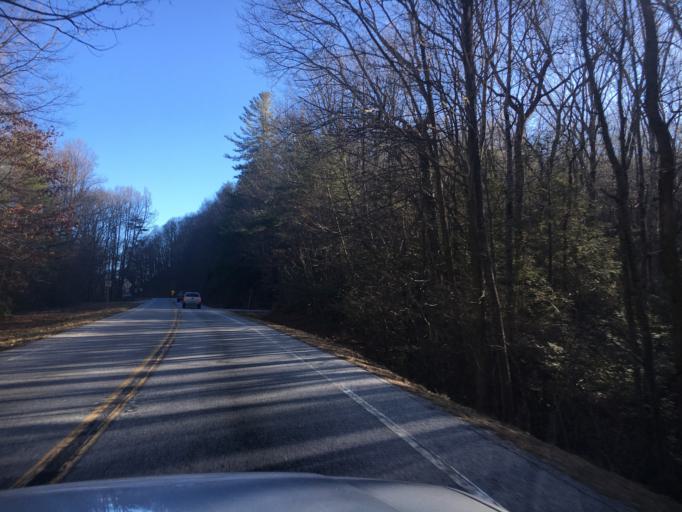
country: US
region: Georgia
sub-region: Union County
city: Blairsville
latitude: 34.7419
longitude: -83.9210
